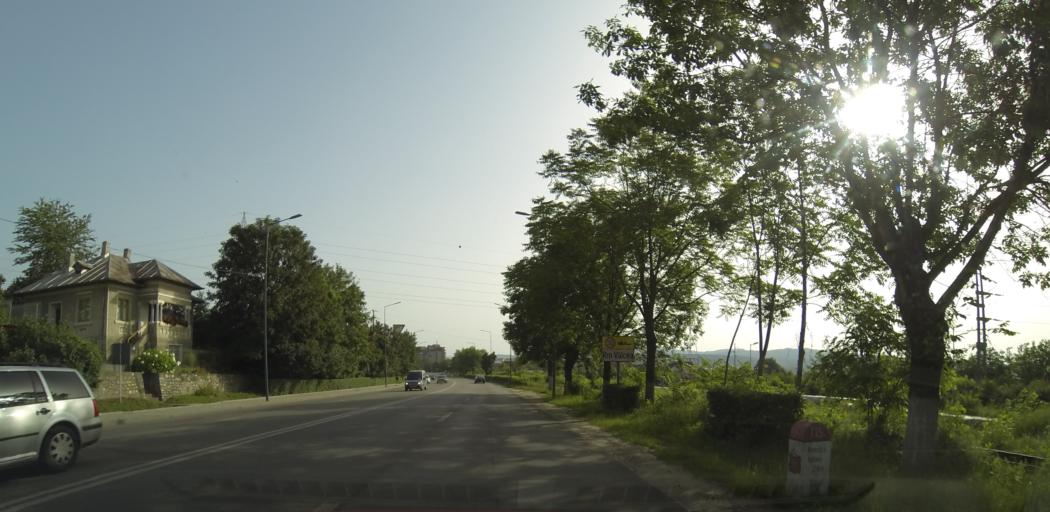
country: RO
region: Valcea
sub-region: Municipiul Ramnicu Valcea
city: Ramnicu Valcea
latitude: 45.0854
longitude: 24.3580
